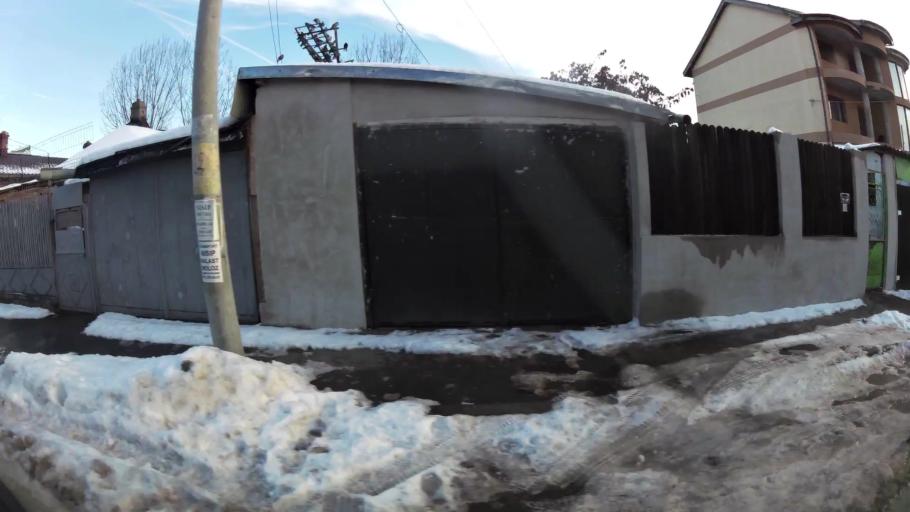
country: RO
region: Bucuresti
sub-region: Municipiul Bucuresti
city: Bucuresti
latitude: 44.3880
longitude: 26.0814
